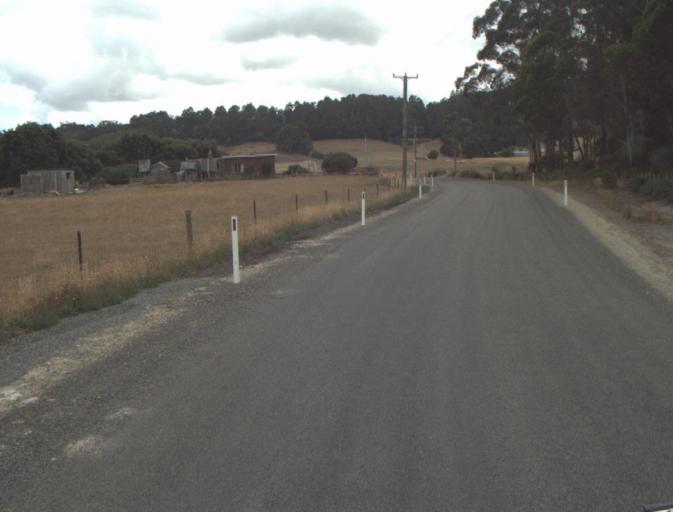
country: AU
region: Tasmania
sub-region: Launceston
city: Mayfield
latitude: -41.2080
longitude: 147.1877
